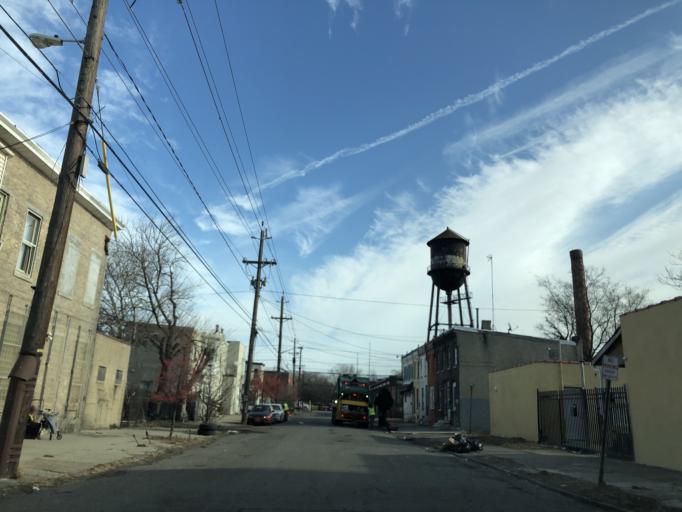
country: US
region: New Jersey
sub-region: Camden County
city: Camden
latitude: 39.9196
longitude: -75.1197
